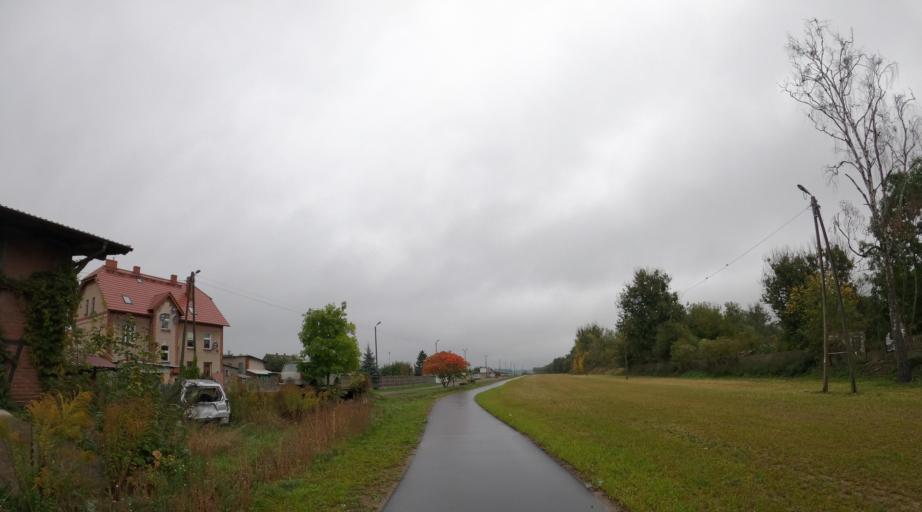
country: PL
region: West Pomeranian Voivodeship
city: Trzcinsko Zdroj
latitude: 52.9625
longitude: 14.6190
